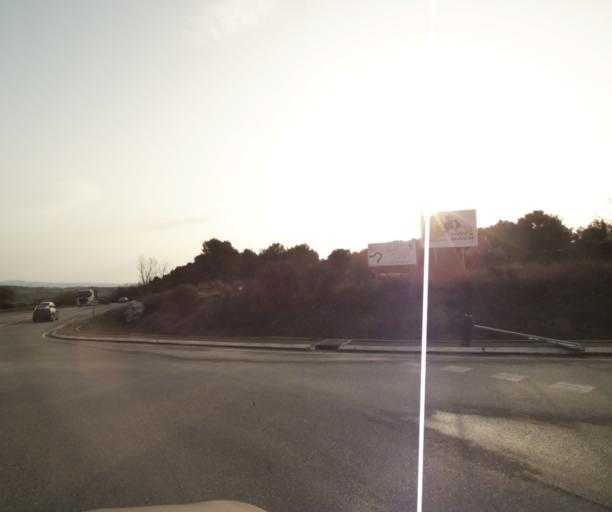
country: FR
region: Provence-Alpes-Cote d'Azur
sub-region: Departement des Bouches-du-Rhone
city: Peynier
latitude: 43.4609
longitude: 5.6284
